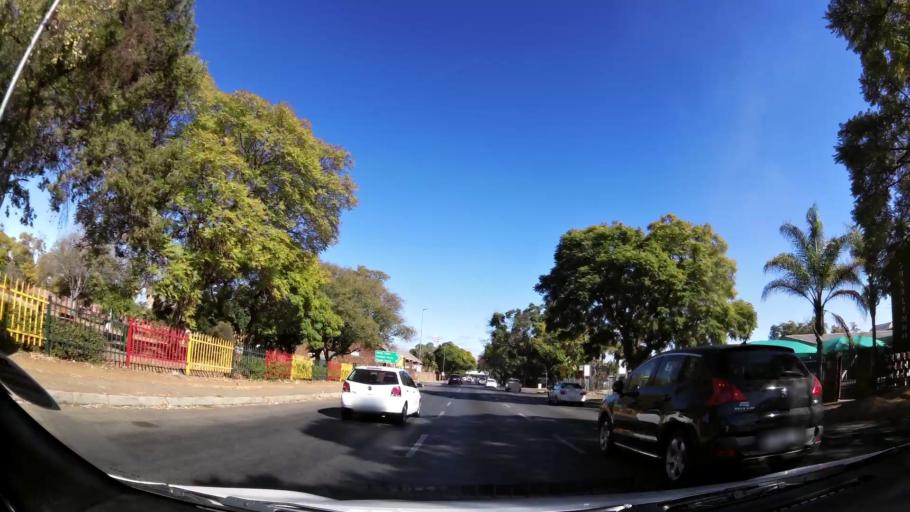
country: ZA
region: Limpopo
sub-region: Capricorn District Municipality
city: Polokwane
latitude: -23.9096
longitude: 29.4624
